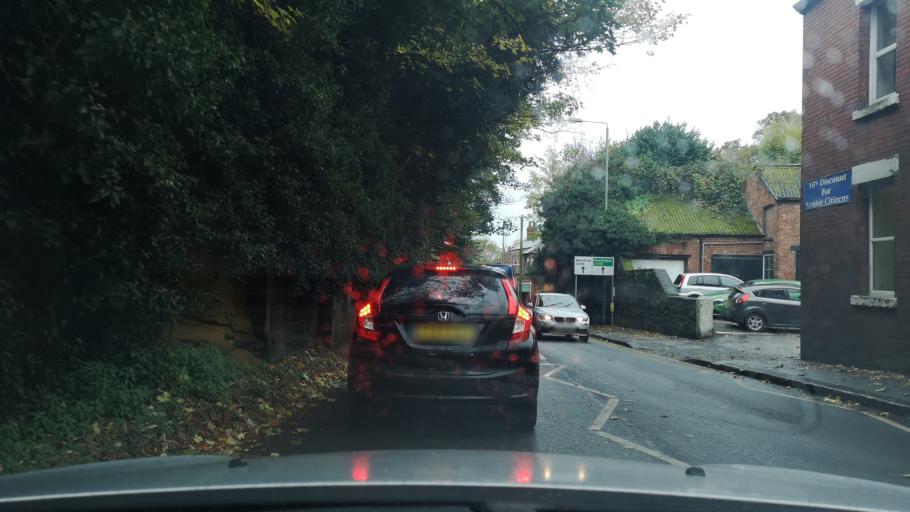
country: GB
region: England
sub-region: City and Borough of Wakefield
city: Pontefract
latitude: 53.6867
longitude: -1.3135
